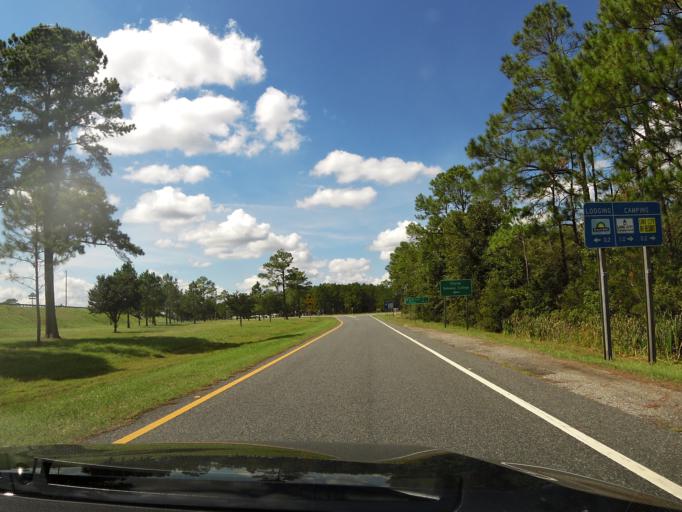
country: US
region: Florida
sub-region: Columbia County
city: Five Points
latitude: 30.2421
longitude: -82.6359
